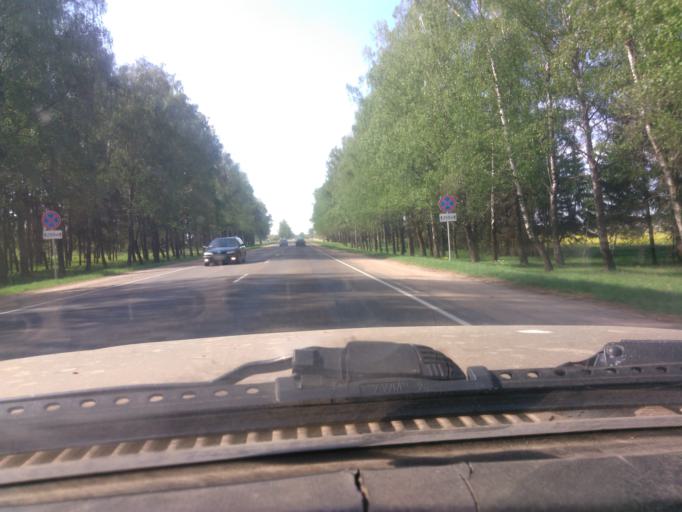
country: BY
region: Mogilev
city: Buynichy
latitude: 53.8434
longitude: 30.2497
